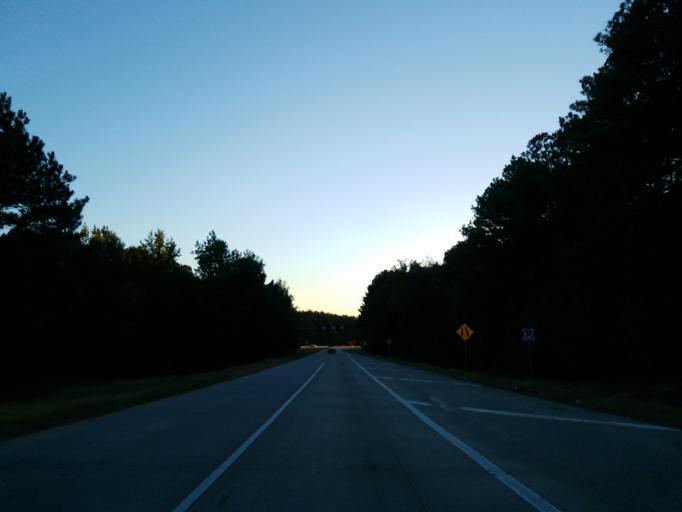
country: US
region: Georgia
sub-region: Forsyth County
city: Cumming
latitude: 34.1587
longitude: -84.1738
